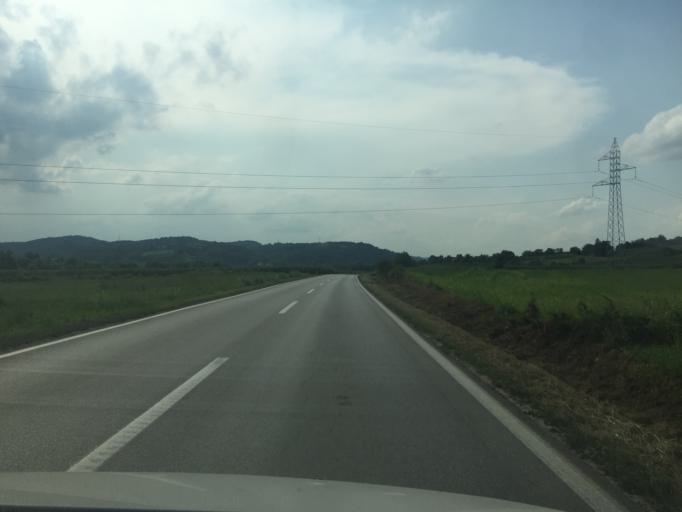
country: BA
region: Federation of Bosnia and Herzegovina
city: Mionica
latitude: 44.7954
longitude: 18.4841
